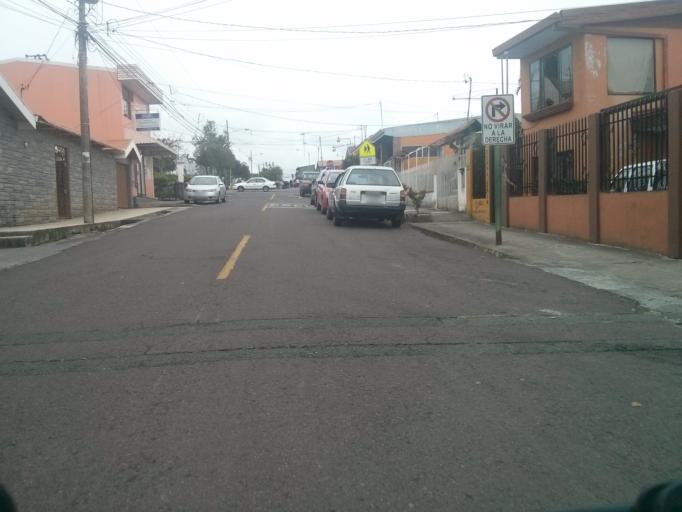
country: CR
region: Heredia
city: Angeles
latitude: 10.0168
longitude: -84.0569
